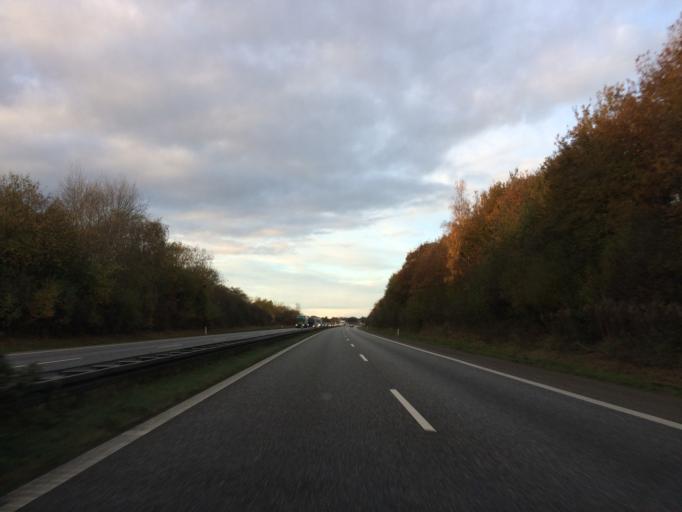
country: DK
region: South Denmark
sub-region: Aabenraa Kommune
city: Rodekro
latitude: 55.0976
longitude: 9.3680
